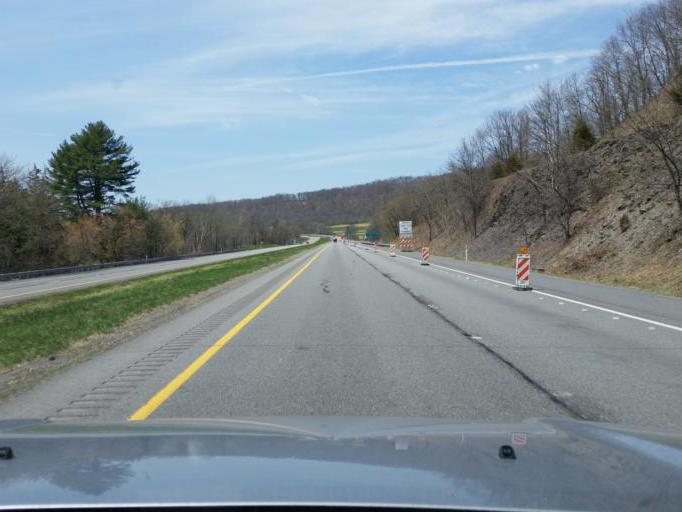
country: US
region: Pennsylvania
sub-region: Perry County
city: Newport
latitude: 40.5657
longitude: -77.1951
